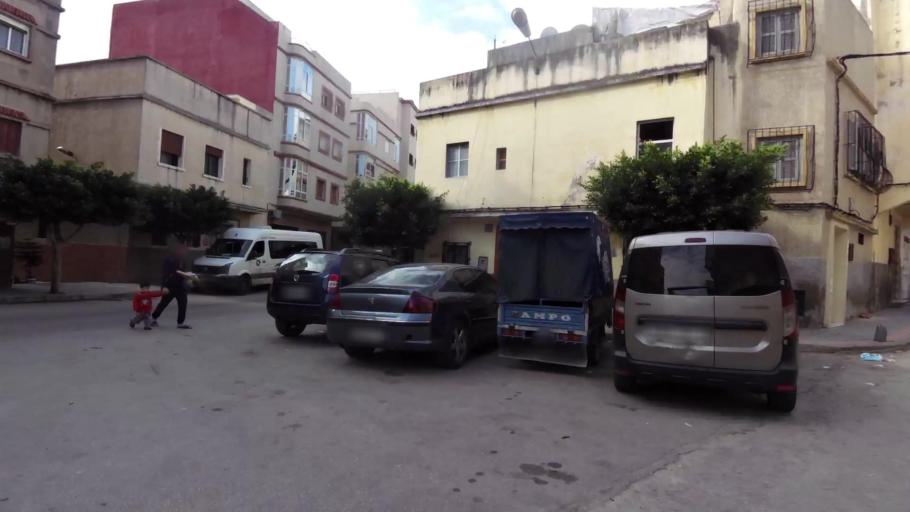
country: MA
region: Tanger-Tetouan
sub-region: Tanger-Assilah
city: Tangier
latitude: 35.7658
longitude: -5.8282
